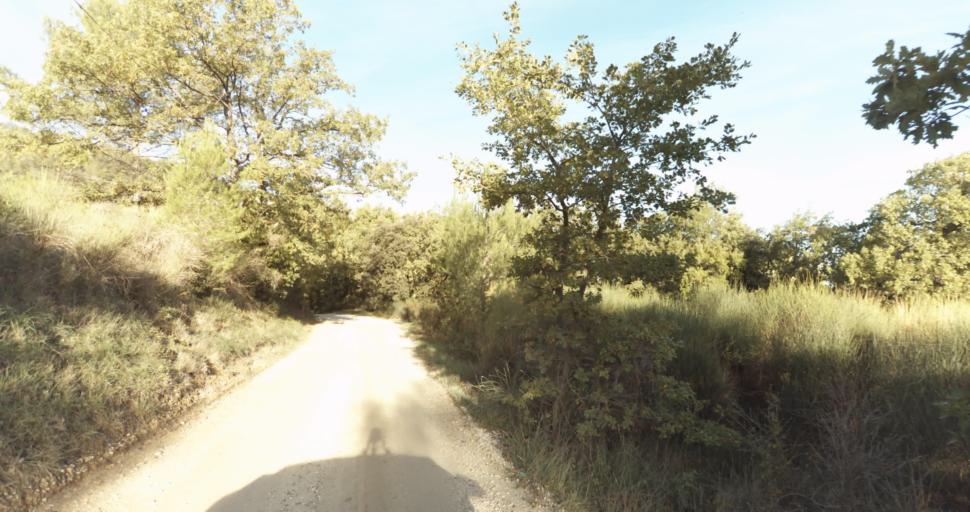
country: FR
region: Provence-Alpes-Cote d'Azur
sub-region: Departement des Bouches-du-Rhone
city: Venelles
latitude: 43.6222
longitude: 5.4671
